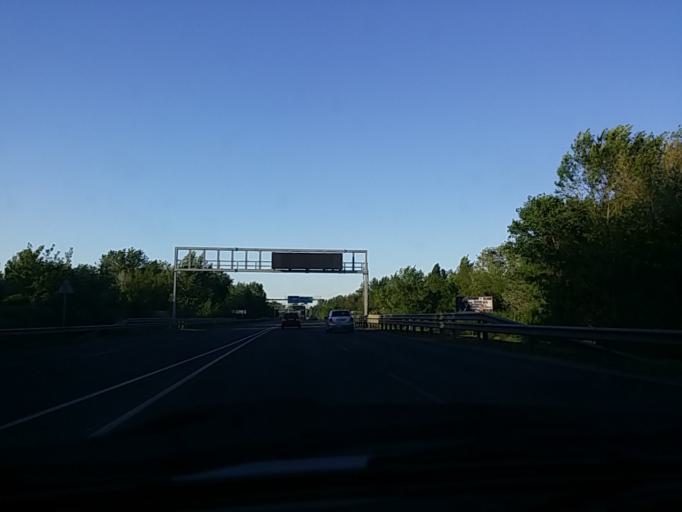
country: HU
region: Budapest
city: Budapest IV. keruelet
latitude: 47.5969
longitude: 19.0970
